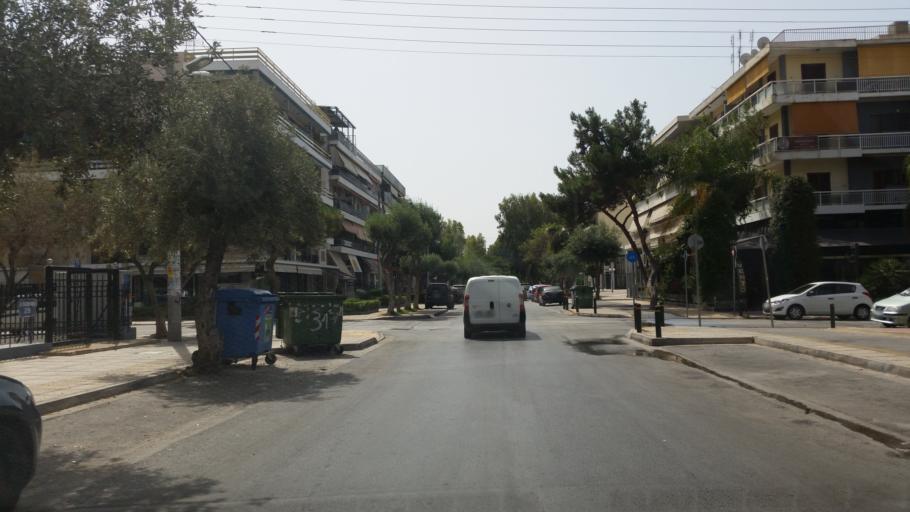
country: GR
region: Attica
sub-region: Nomarchia Athinas
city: Glyfada
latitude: 37.8624
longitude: 23.7498
